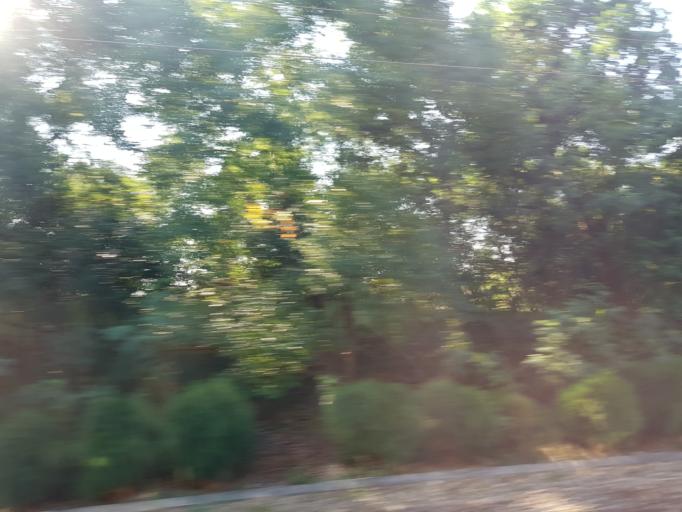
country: TW
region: Taiwan
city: Fengyuan
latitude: 24.2904
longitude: 120.7330
